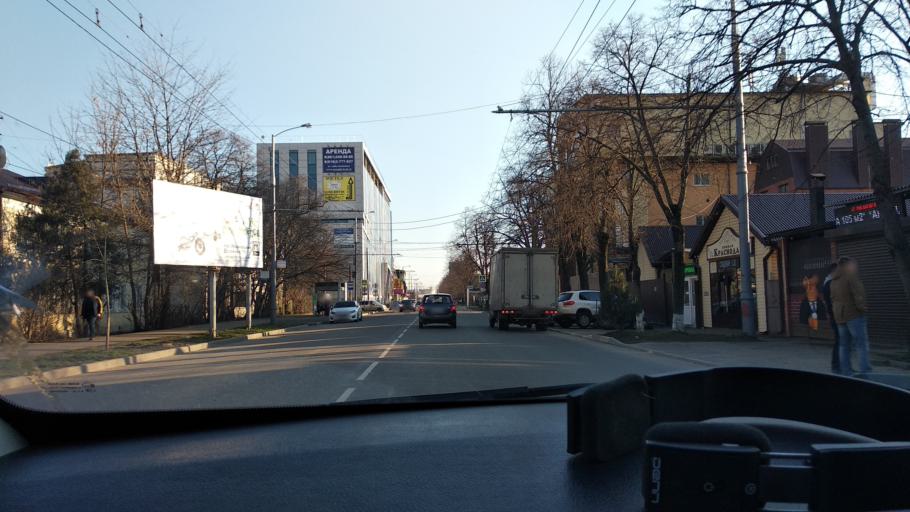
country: RU
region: Adygeya
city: Yablonovskiy
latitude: 45.0049
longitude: 38.9608
